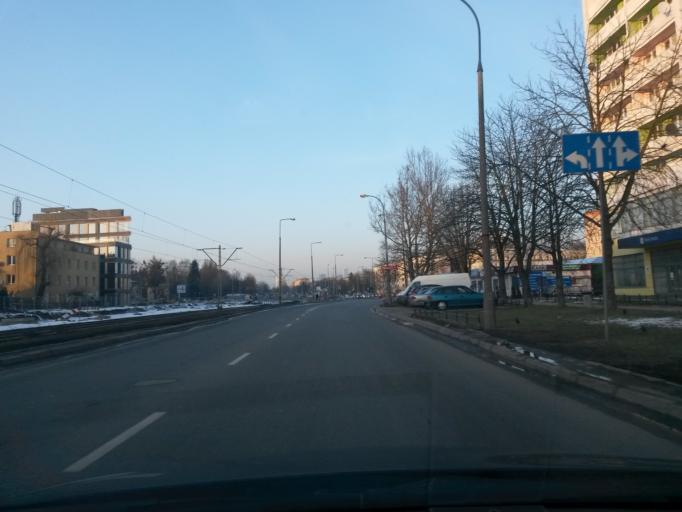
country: PL
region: Masovian Voivodeship
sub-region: Warszawa
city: Ochota
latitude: 52.1937
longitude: 21.0020
